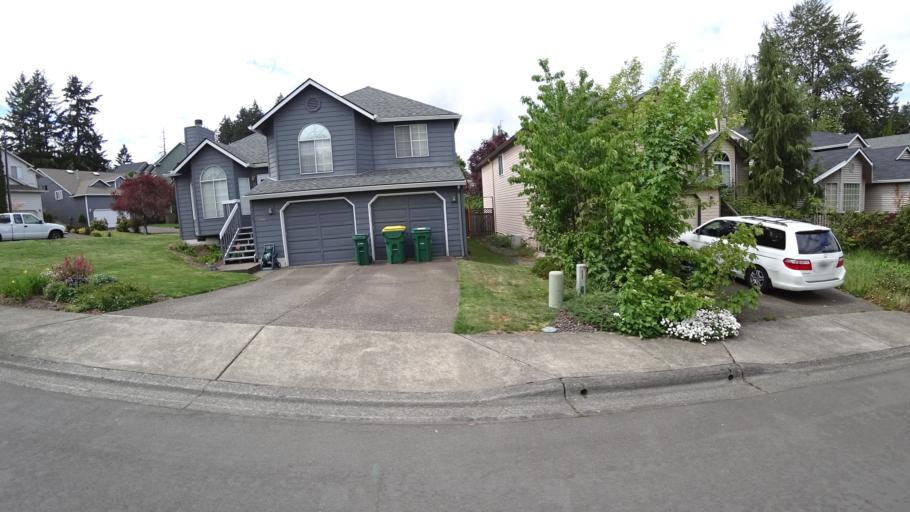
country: US
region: Oregon
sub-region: Washington County
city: Aloha
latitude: 45.4682
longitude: -122.8588
